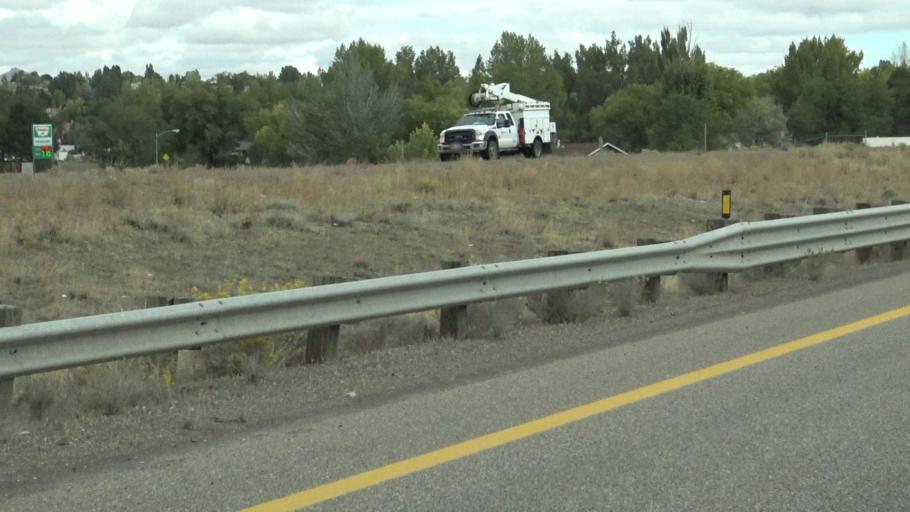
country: US
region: Nevada
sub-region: Elko County
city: Elko
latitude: 40.8401
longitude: -115.7766
